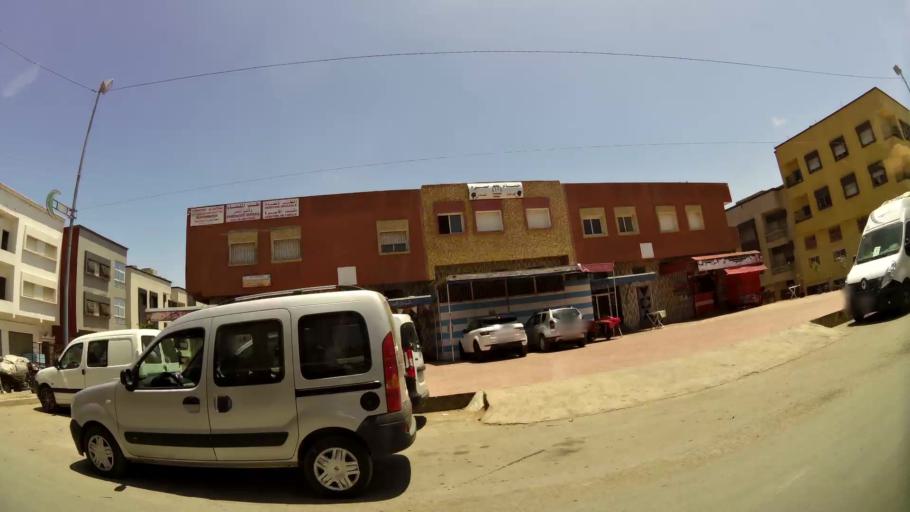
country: MA
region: Gharb-Chrarda-Beni Hssen
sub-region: Kenitra Province
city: Kenitra
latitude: 34.2624
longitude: -6.6439
